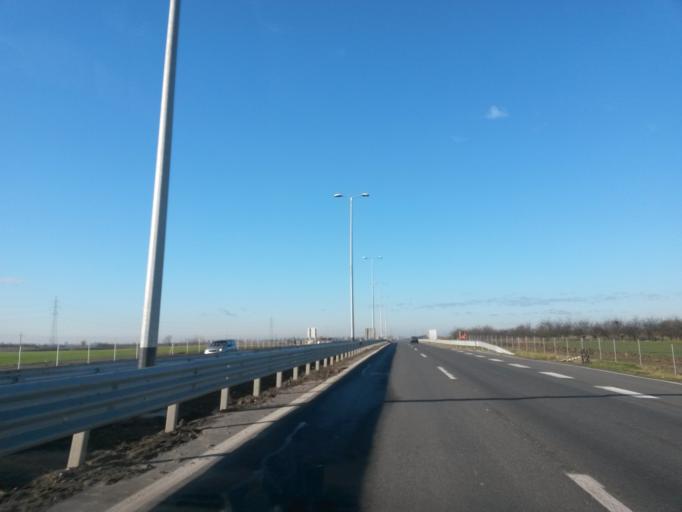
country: HR
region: Osjecko-Baranjska
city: Visnjevac
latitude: 45.5544
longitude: 18.6283
